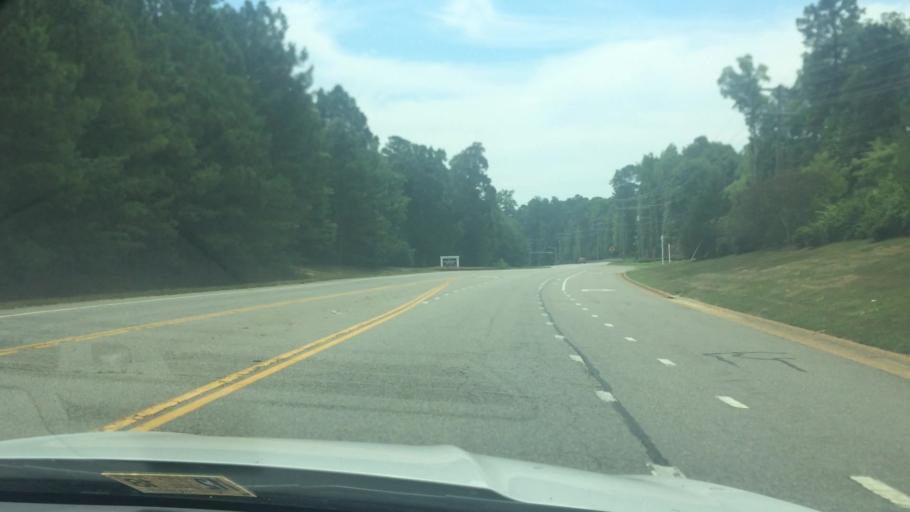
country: US
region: Virginia
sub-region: James City County
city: Williamsburg
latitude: 37.2667
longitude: -76.8058
